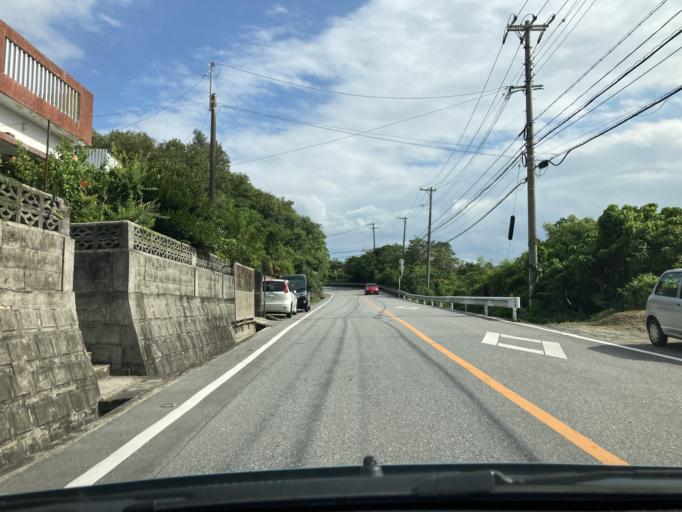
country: JP
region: Okinawa
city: Ginowan
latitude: 26.2699
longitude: 127.7820
